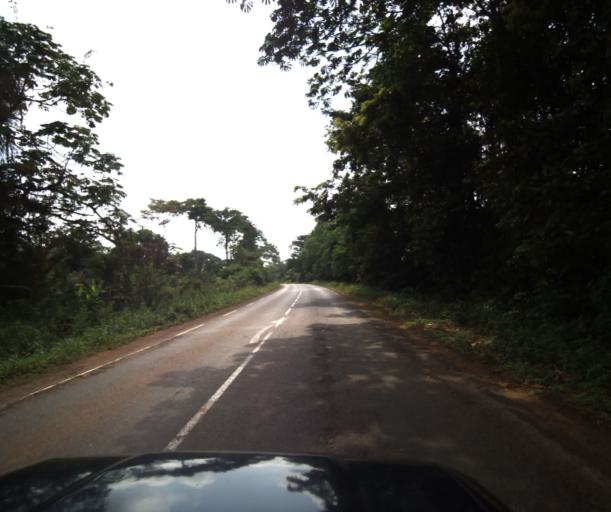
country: CM
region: Centre
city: Eseka
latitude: 3.8904
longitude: 10.7843
